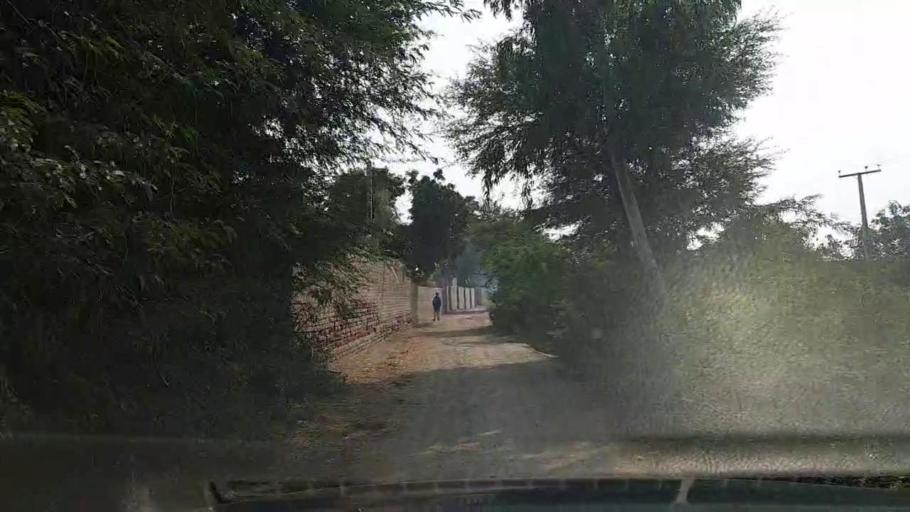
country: PK
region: Sindh
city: Mirpur Batoro
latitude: 24.6954
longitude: 68.2193
